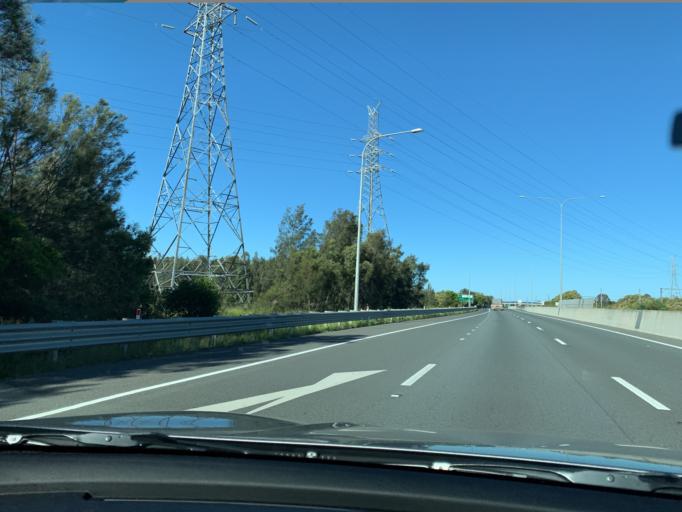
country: AU
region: Queensland
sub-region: Brisbane
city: Cannon Hill
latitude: -27.4500
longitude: 153.1190
